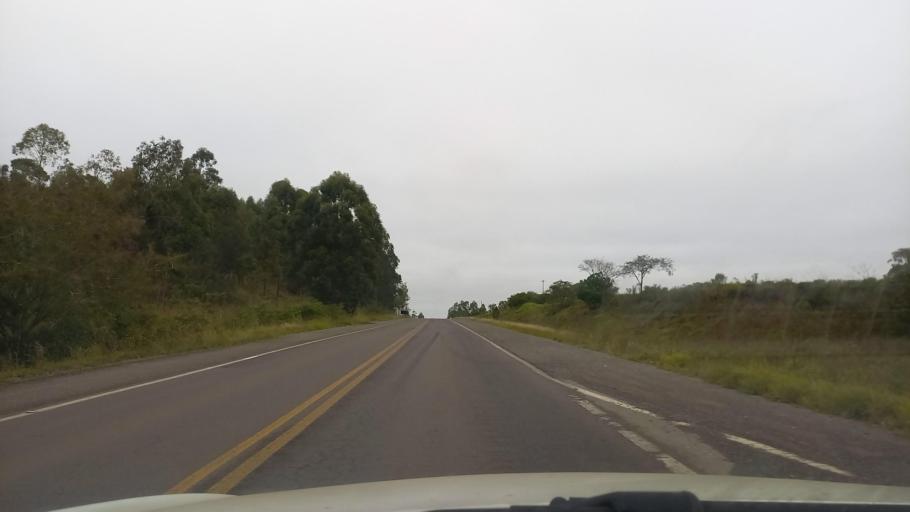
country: BR
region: Rio Grande do Sul
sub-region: Sao Pedro Do Sul
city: Sao Pedro do Sul
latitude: -29.7723
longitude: -54.0957
